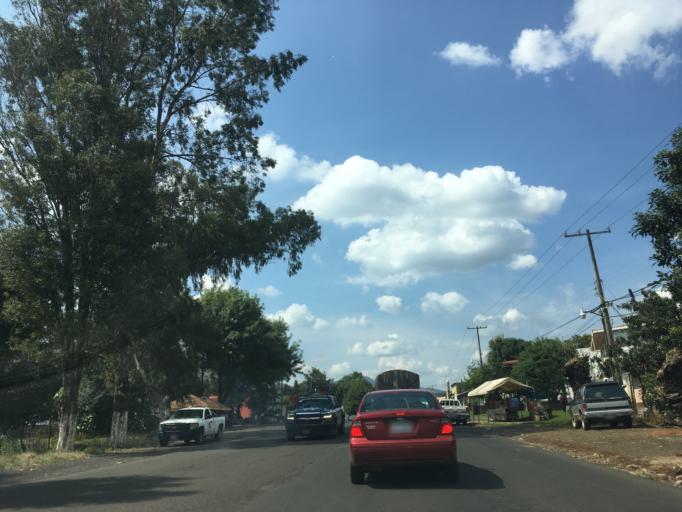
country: MX
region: Michoacan
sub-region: Tingueindin
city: Tingueindin
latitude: 19.7722
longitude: -102.4989
